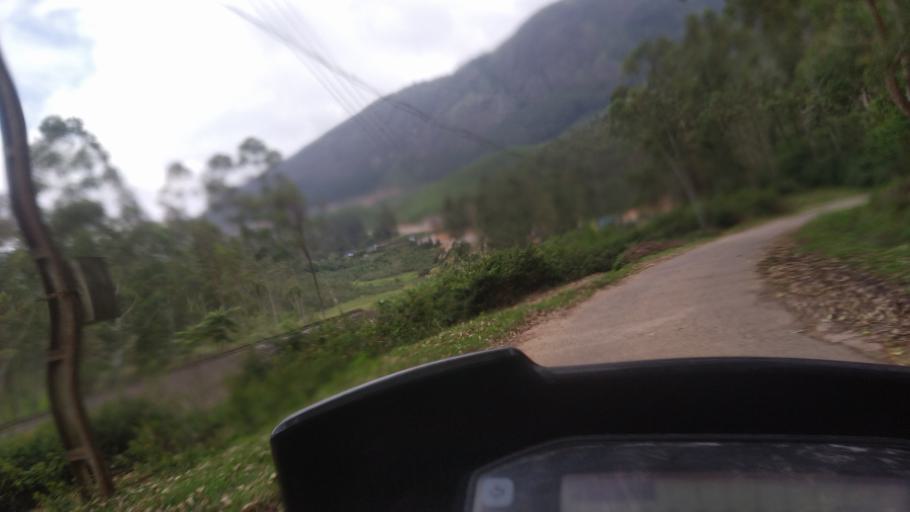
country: IN
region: Kerala
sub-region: Idukki
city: Munnar
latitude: 10.0547
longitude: 77.1105
